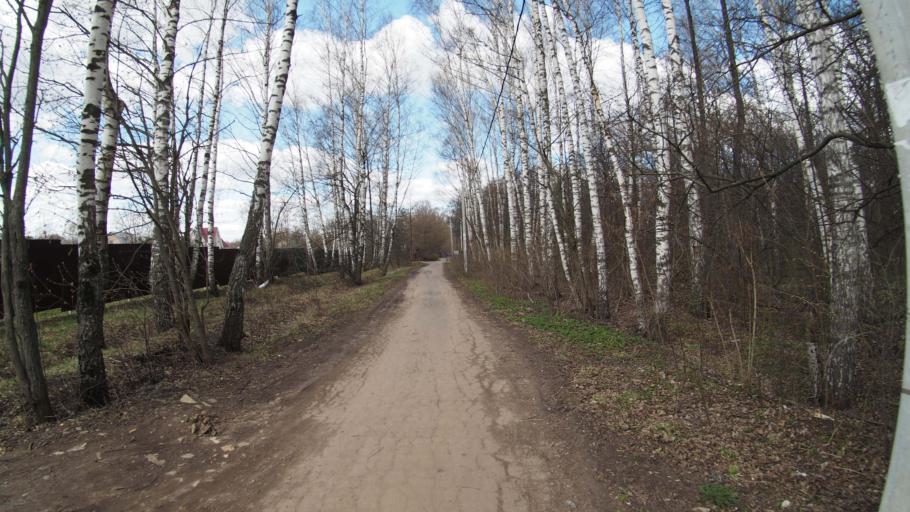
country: RU
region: Moskovskaya
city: Malyshevo
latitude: 55.5457
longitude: 38.3026
